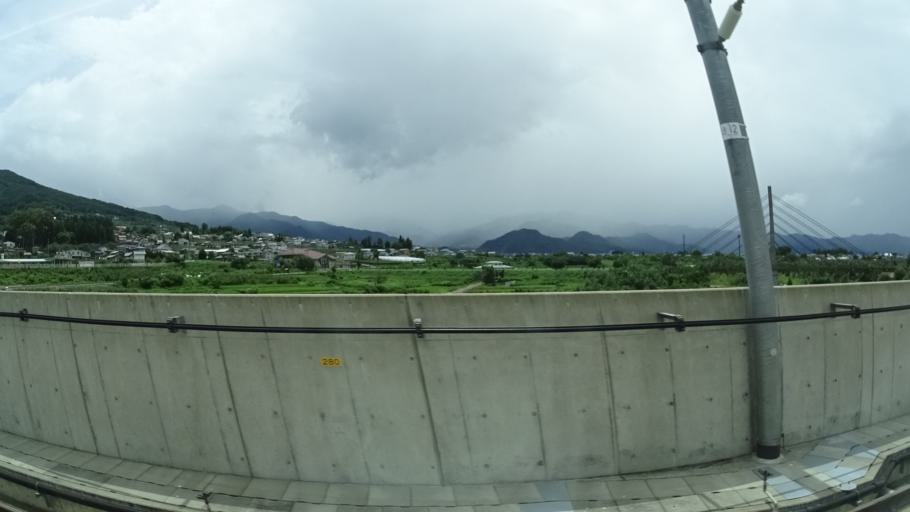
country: JP
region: Nagano
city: Nakano
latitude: 36.7936
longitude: 138.3622
